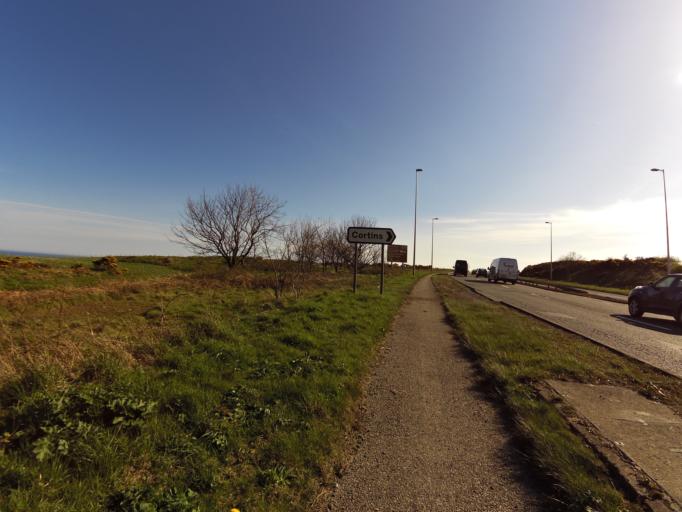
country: GB
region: Scotland
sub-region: Aberdeenshire
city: Newtonhill
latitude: 57.0058
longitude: -2.1740
